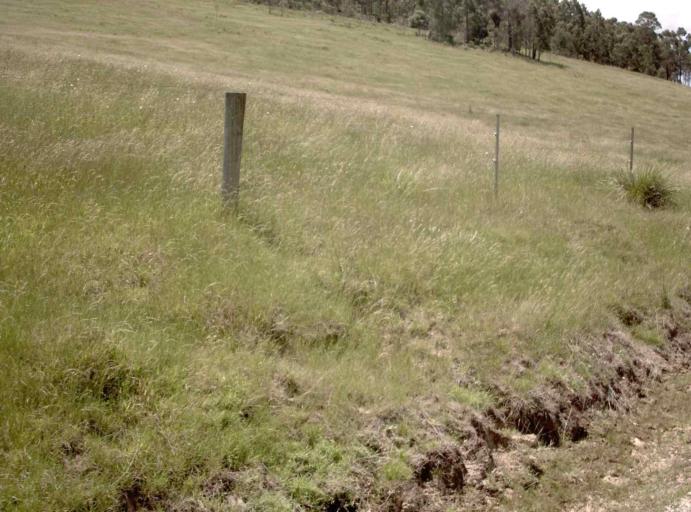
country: AU
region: New South Wales
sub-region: Bombala
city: Bombala
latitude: -37.3580
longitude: 149.0264
